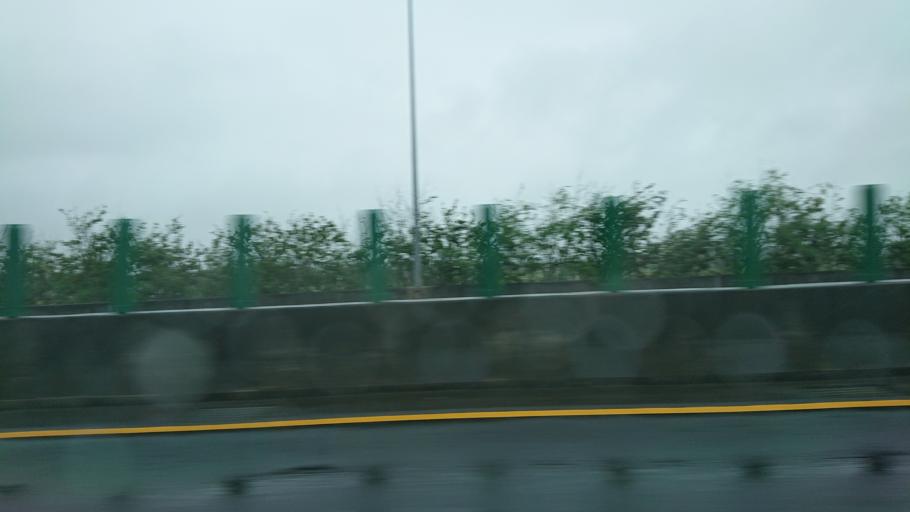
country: TW
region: Taiwan
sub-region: Chiayi
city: Taibao
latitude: 23.6494
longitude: 120.1689
